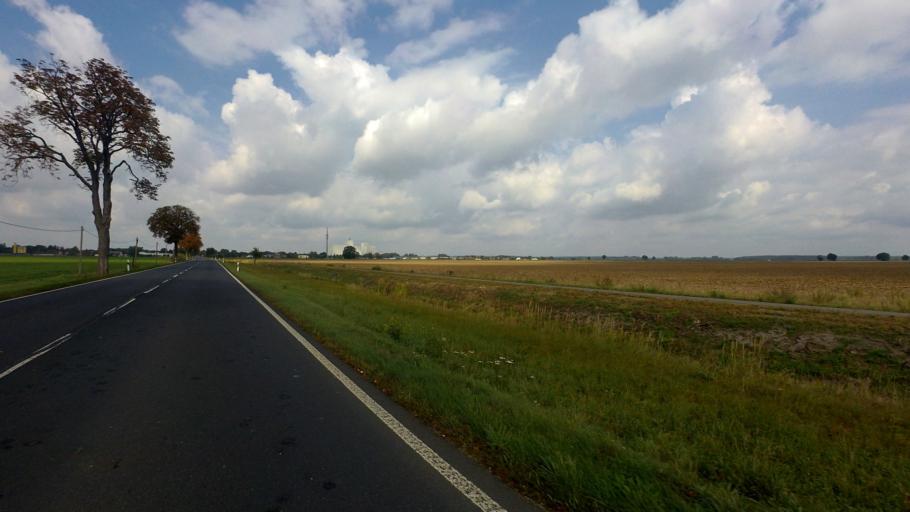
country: DE
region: Brandenburg
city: Herzberg
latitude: 51.6831
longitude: 13.2597
